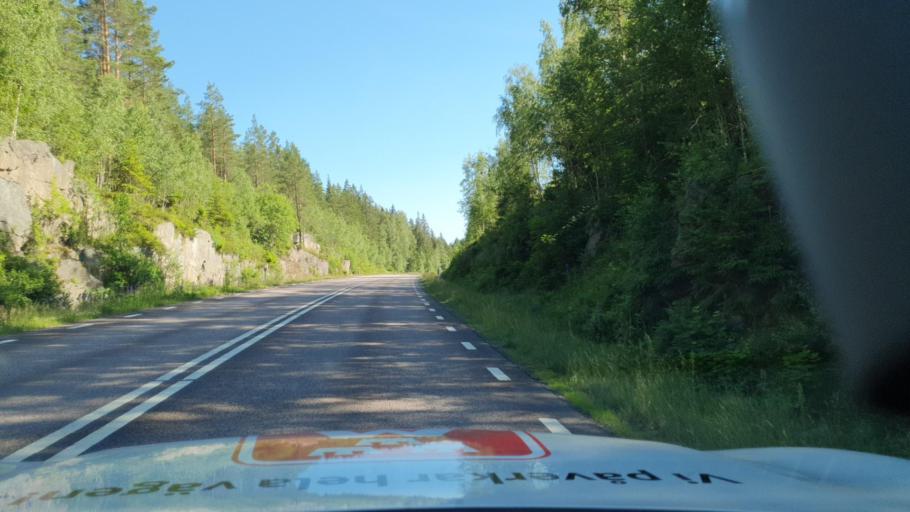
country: SE
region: OErebro
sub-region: Karlskoga Kommun
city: Karlskoga
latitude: 59.4259
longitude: 14.4273
